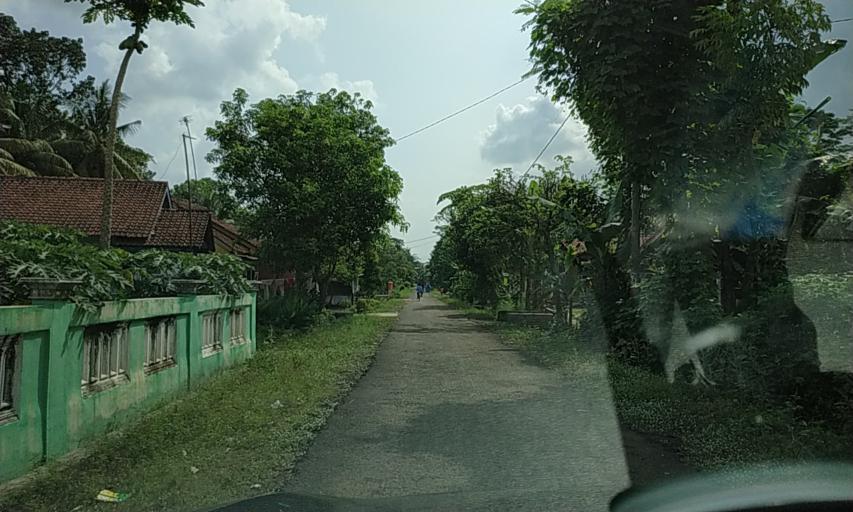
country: ID
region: Central Java
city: Bakung
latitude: -7.3498
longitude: 108.6628
